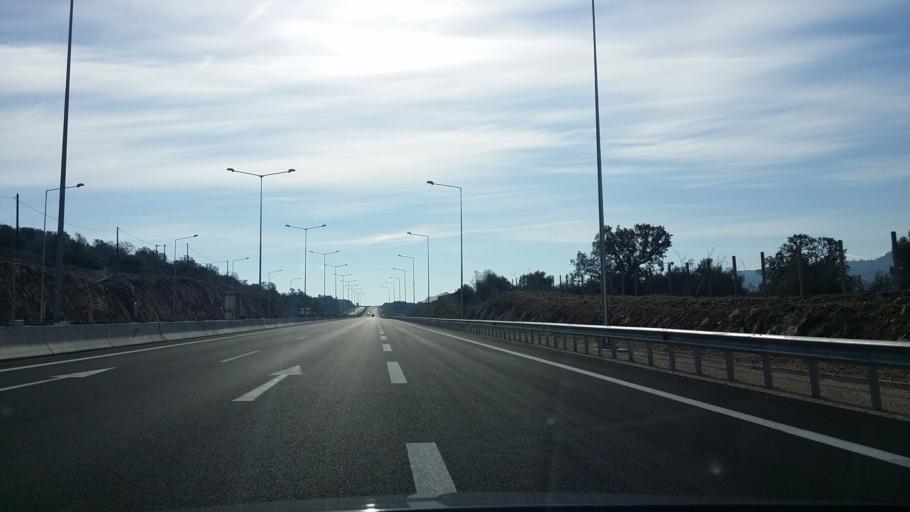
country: GR
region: West Greece
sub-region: Nomos Aitolias kai Akarnanias
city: Fitiai
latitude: 38.7459
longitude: 21.2044
